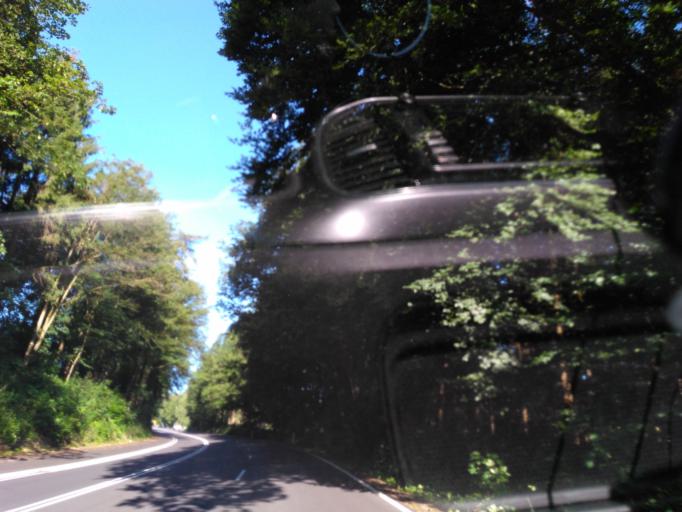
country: DE
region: North Rhine-Westphalia
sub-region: Regierungsbezirk Koln
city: Overath
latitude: 50.9393
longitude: 7.2675
